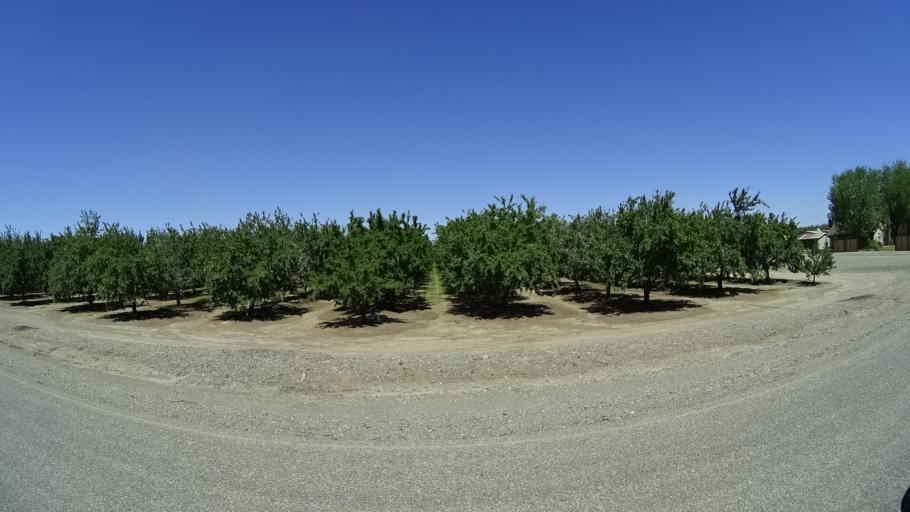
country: US
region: California
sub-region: Glenn County
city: Orland
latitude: 39.7249
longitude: -122.1142
